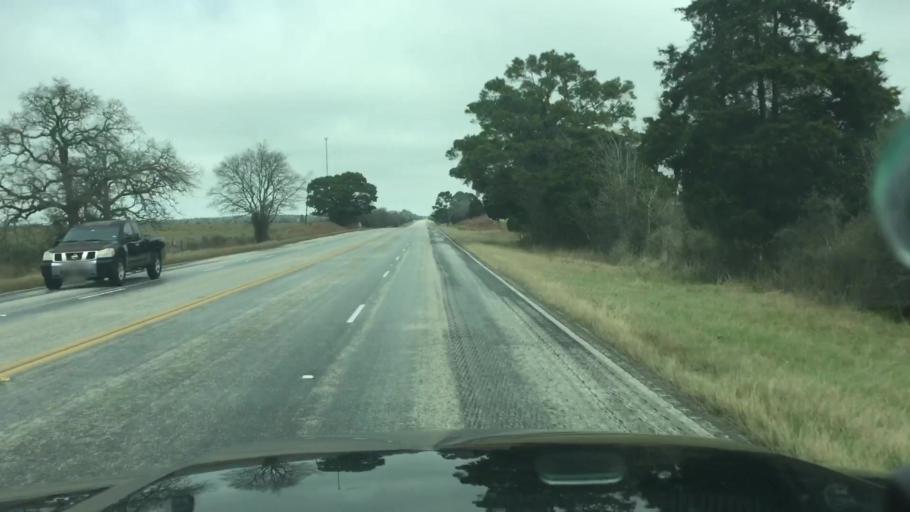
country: US
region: Texas
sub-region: Lee County
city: Giddings
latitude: 30.1005
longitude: -96.9136
